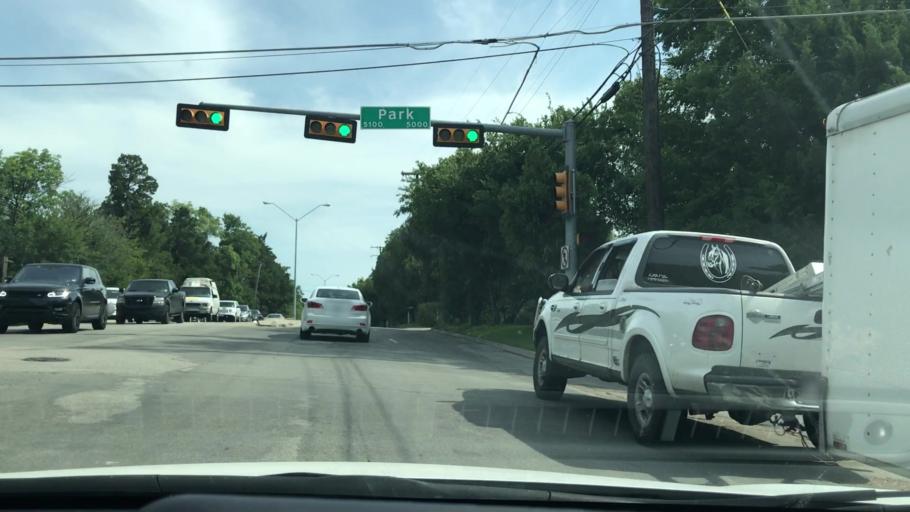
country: US
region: Texas
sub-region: Dallas County
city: University Park
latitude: 32.8742
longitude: -96.8213
